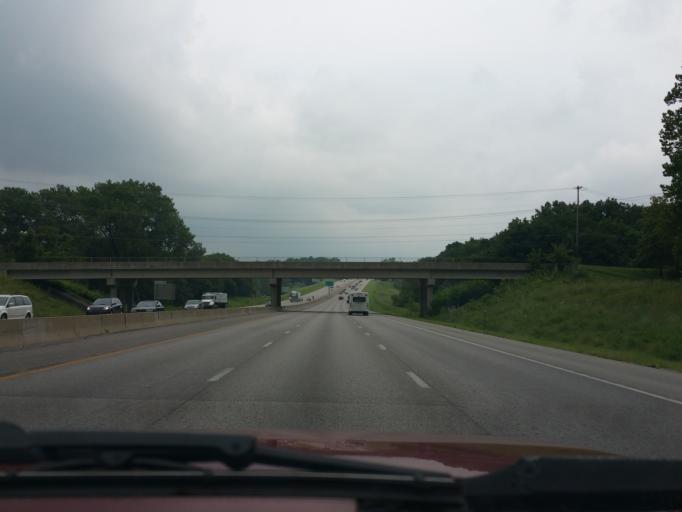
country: US
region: Kansas
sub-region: Johnson County
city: Shawnee
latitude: 39.1060
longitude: -94.7300
